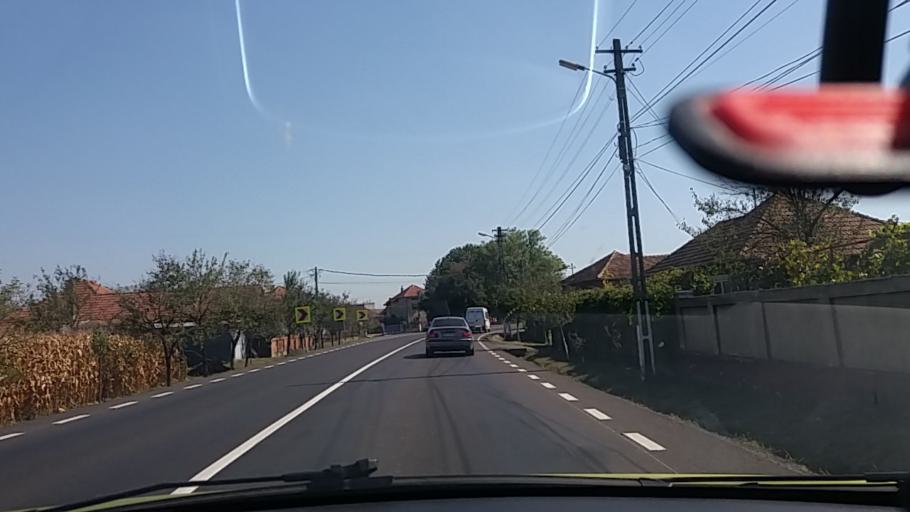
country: RO
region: Hunedoara
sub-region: Comuna Ilia
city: Ilia
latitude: 45.9402
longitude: 22.6478
